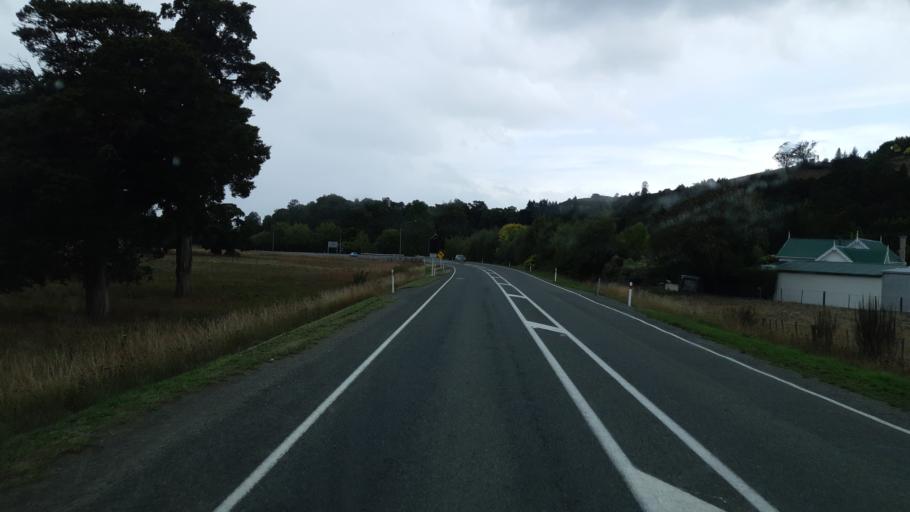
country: NZ
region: Tasman
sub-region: Tasman District
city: Wakefield
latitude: -41.4084
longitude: 173.0342
